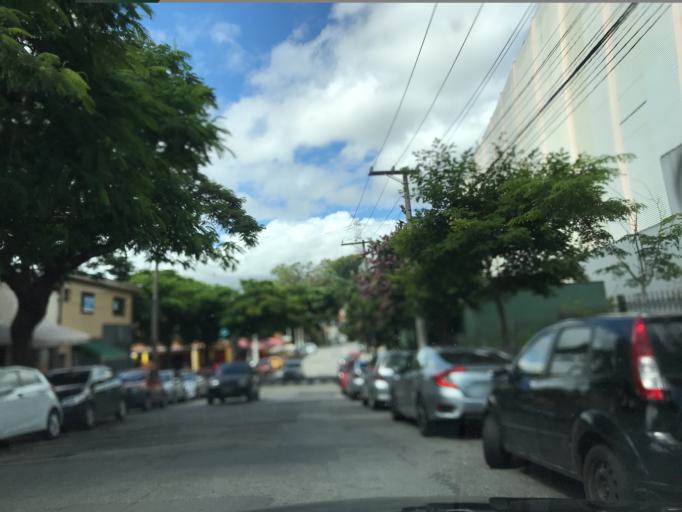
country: BR
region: Sao Paulo
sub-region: Osasco
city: Osasco
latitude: -23.5475
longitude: -46.7582
